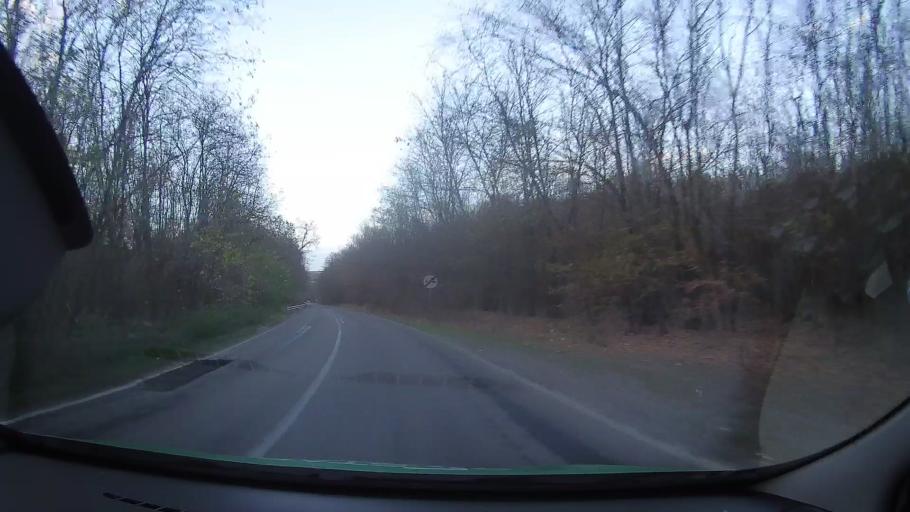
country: RO
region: Constanta
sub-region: Comuna Baneasa
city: Baneasa
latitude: 44.0825
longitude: 27.6677
